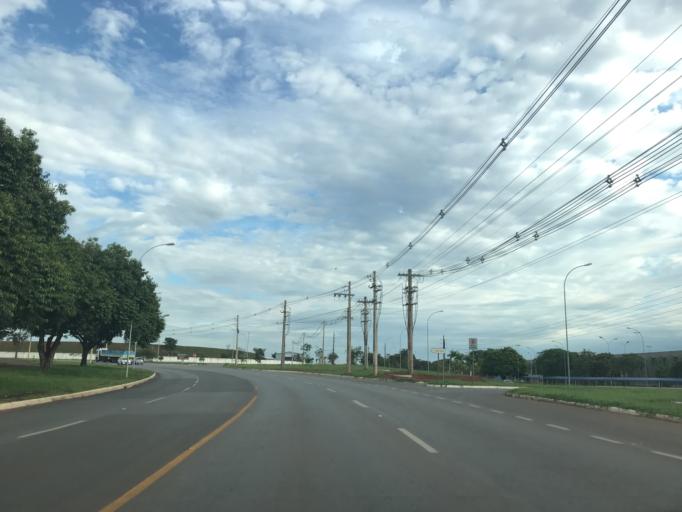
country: BR
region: Federal District
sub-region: Brasilia
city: Brasilia
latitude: -15.7825
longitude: -47.8947
